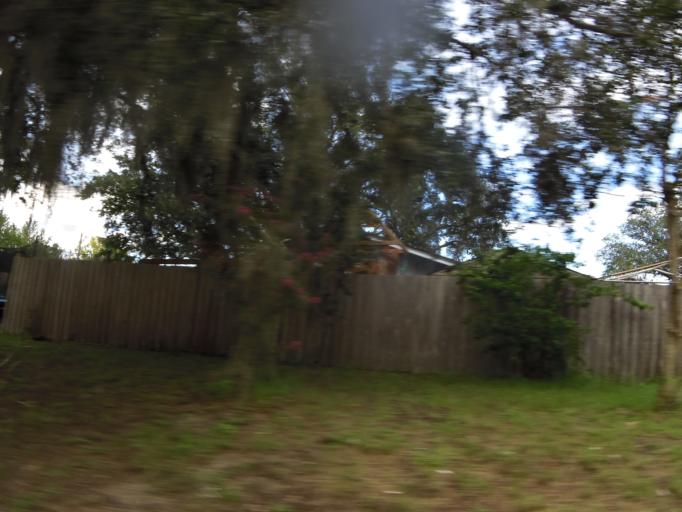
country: US
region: Florida
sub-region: Clay County
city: Lakeside
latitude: 30.1285
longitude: -81.7669
